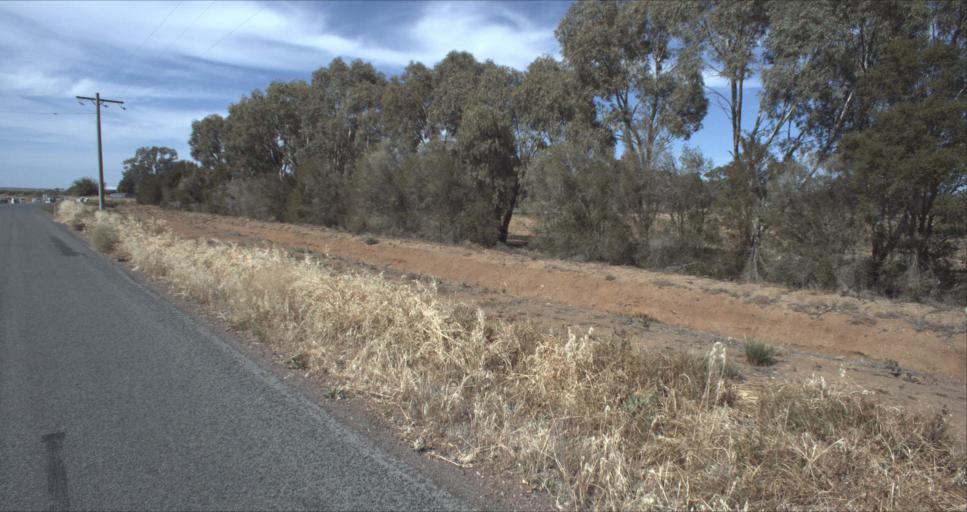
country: AU
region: New South Wales
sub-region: Leeton
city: Leeton
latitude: -34.5739
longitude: 146.4672
